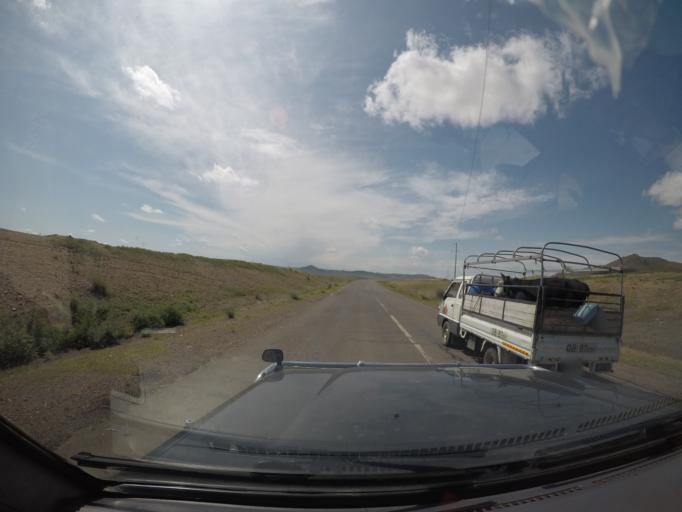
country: MN
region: Hentiy
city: Moron
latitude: 47.3788
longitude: 110.4052
